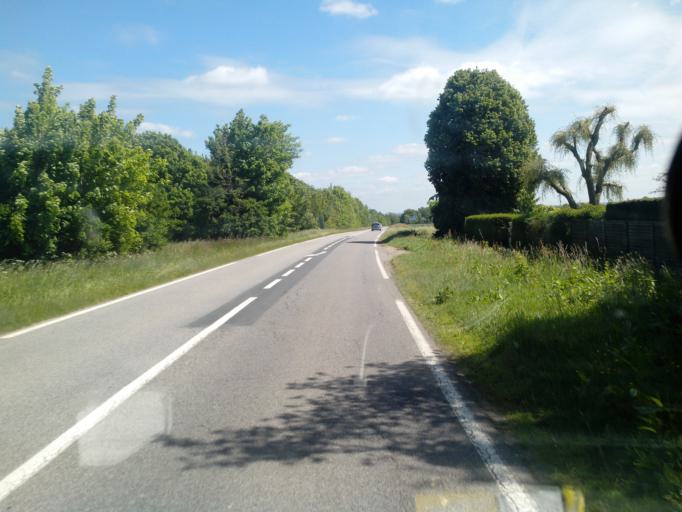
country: FR
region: Haute-Normandie
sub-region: Departement de la Seine-Maritime
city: Tancarville
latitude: 49.4961
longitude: 0.4366
